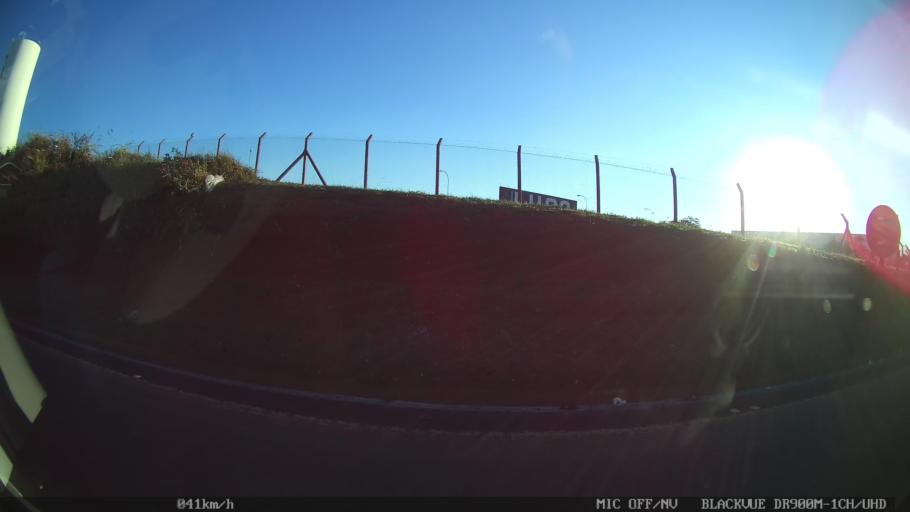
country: BR
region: Sao Paulo
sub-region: Araraquara
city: Araraquara
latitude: -21.7890
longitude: -48.2200
